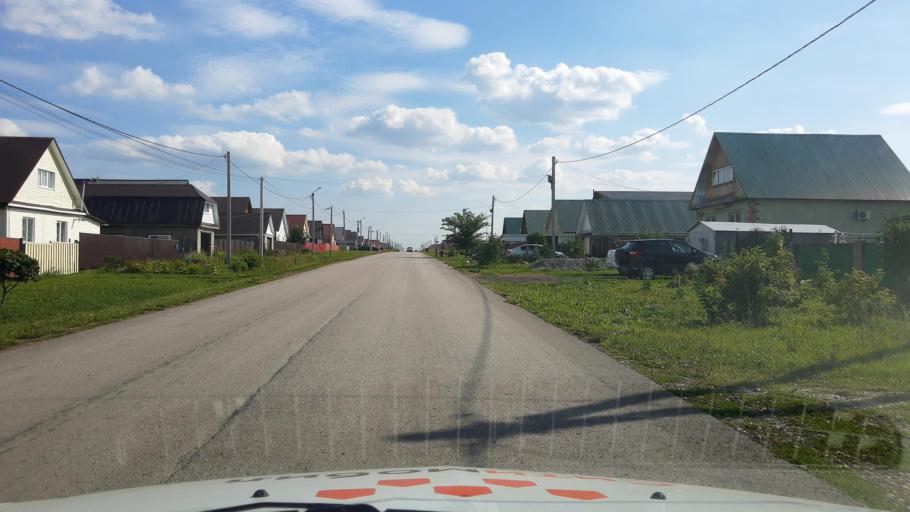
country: RU
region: Bashkortostan
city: Kabakovo
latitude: 54.6551
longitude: 56.2141
